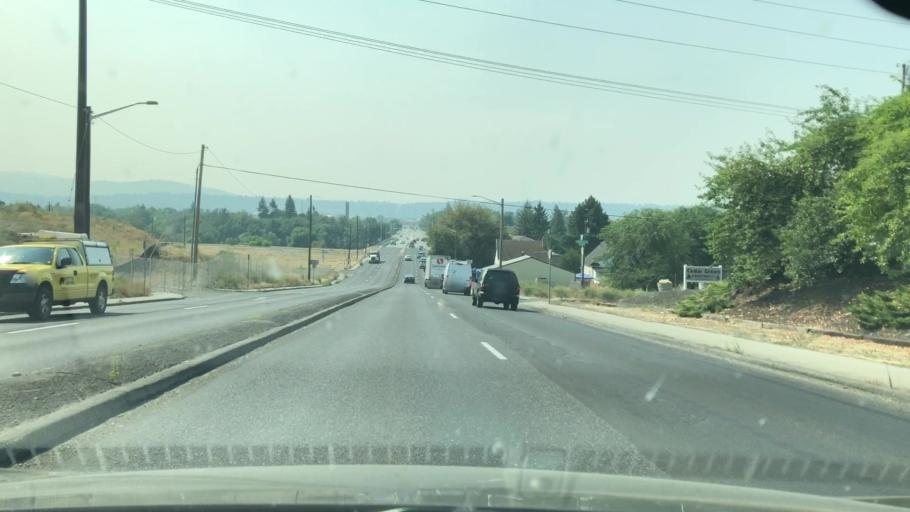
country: US
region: Washington
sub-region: Spokane County
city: Spokane
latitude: 47.6820
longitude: -117.3636
